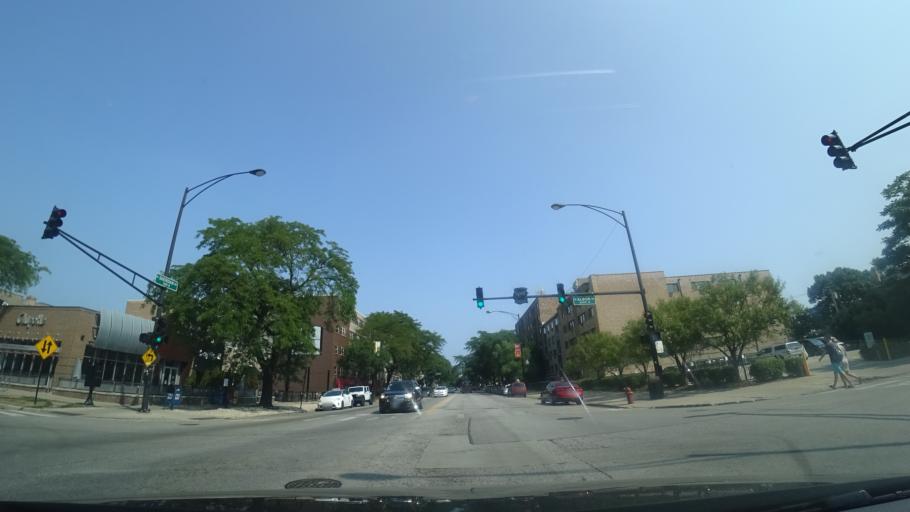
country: US
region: Illinois
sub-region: Cook County
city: Evanston
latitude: 42.0025
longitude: -87.6608
